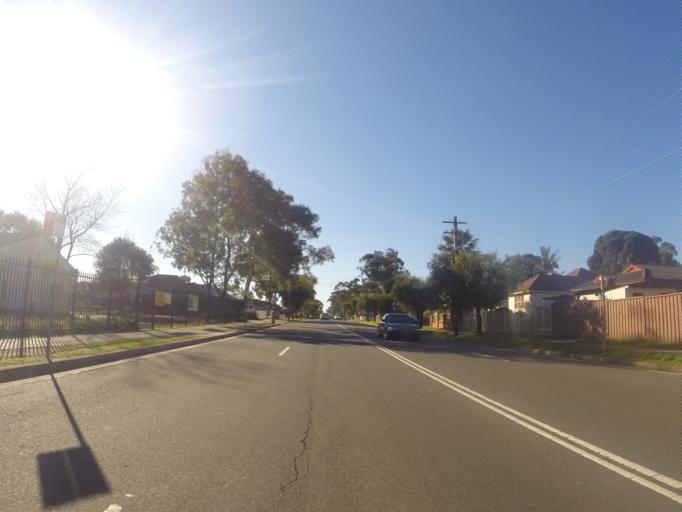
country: AU
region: New South Wales
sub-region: Bankstown
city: Regents Park
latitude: -33.8957
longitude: 151.0212
